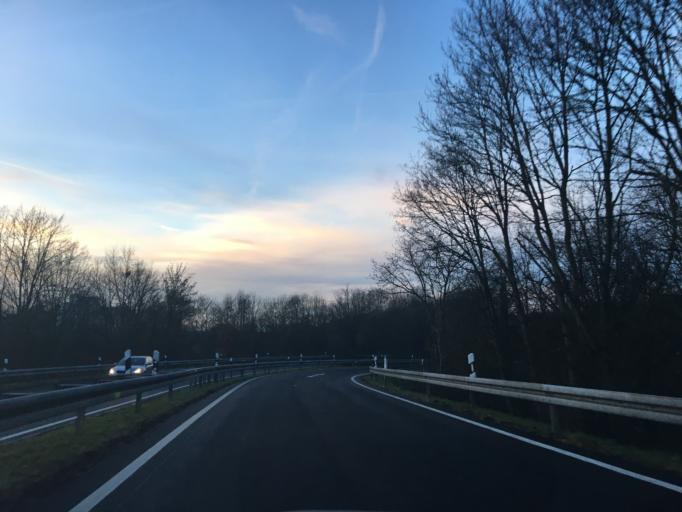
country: DE
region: North Rhine-Westphalia
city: Sankt Augustin
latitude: 50.7870
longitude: 7.1972
